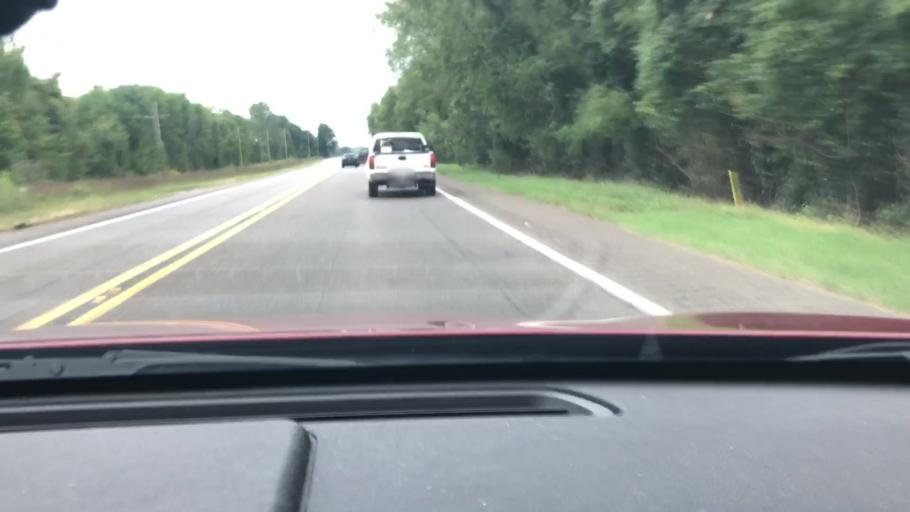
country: US
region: Arkansas
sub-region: Lafayette County
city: Lewisville
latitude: 33.3551
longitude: -93.6649
